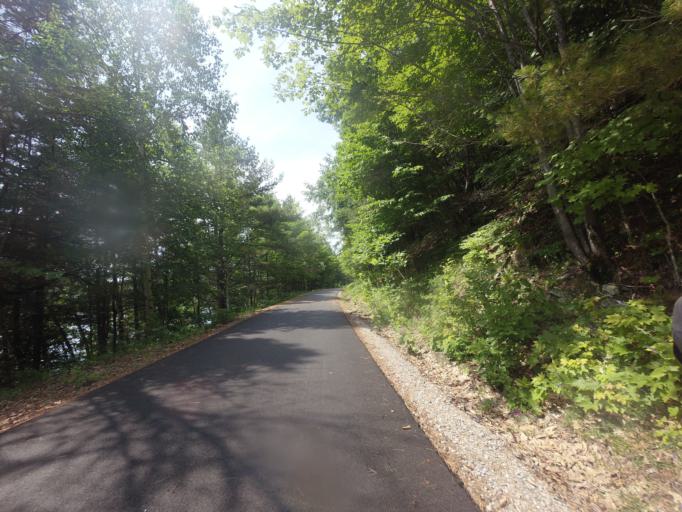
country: CA
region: Quebec
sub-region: Outaouais
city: Maniwaki
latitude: 46.1384
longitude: -76.0337
